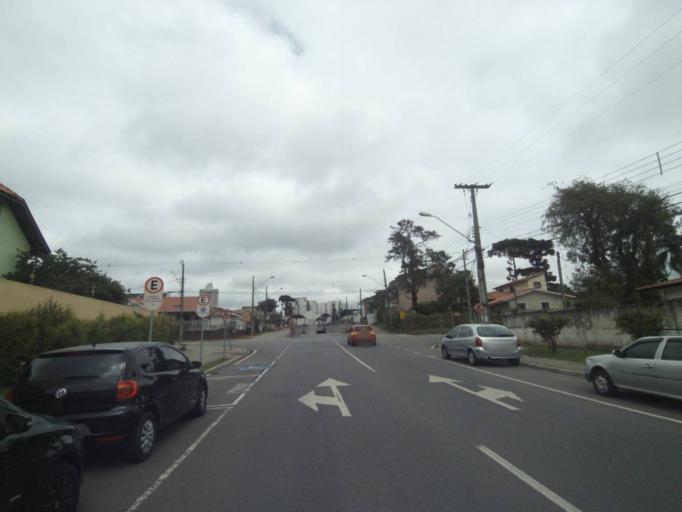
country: BR
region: Parana
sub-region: Pinhais
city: Pinhais
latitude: -25.4358
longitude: -49.2314
